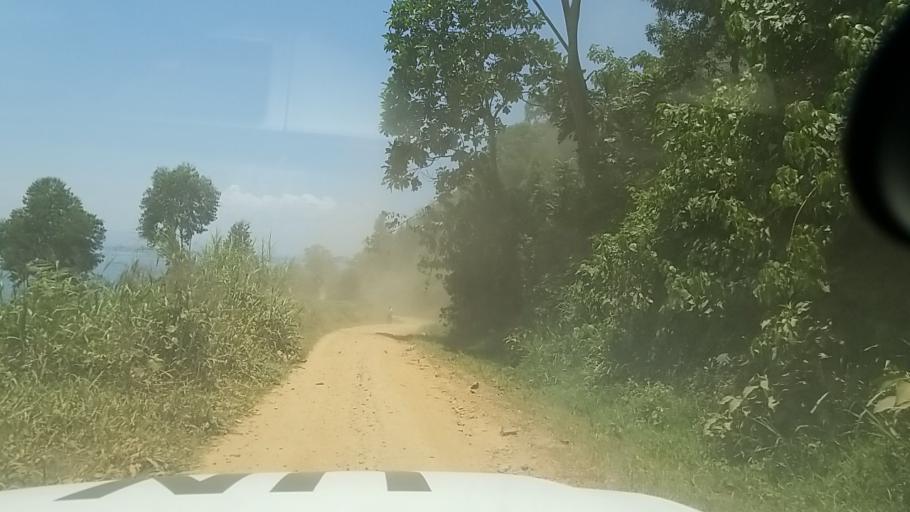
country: CD
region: Nord Kivu
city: Sake
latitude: -1.8350
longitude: 29.0016
